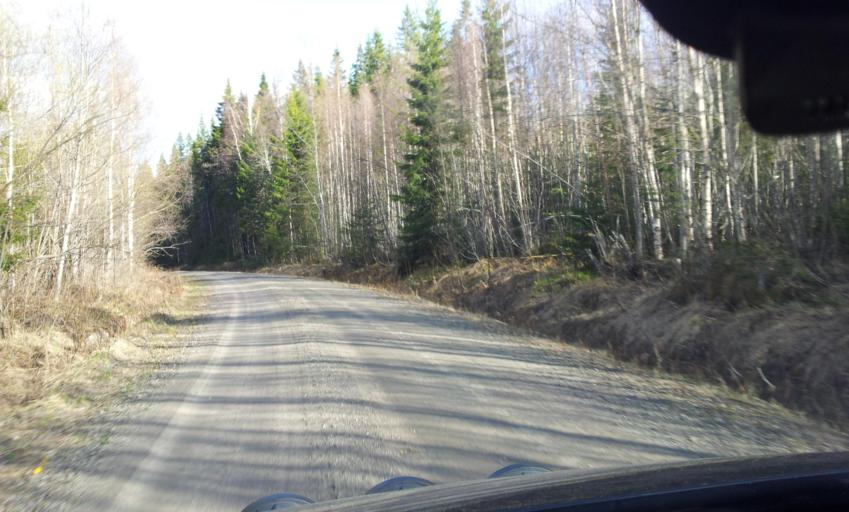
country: SE
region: Vaesternorrland
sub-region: Ange Kommun
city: Ange
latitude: 62.2122
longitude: 15.4150
